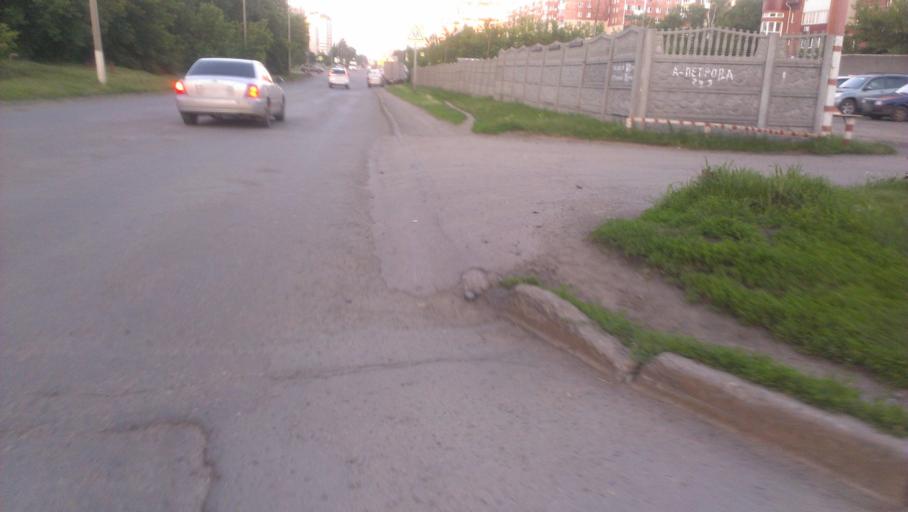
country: RU
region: Altai Krai
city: Novosilikatnyy
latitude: 53.3630
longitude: 83.6650
